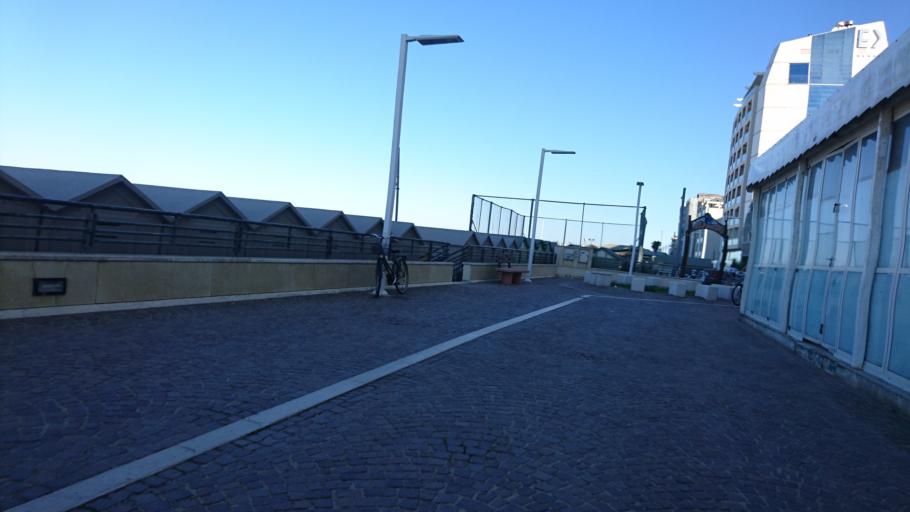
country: IT
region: The Marches
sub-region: Provincia di Pesaro e Urbino
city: Pesaro
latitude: 43.9120
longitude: 12.9217
